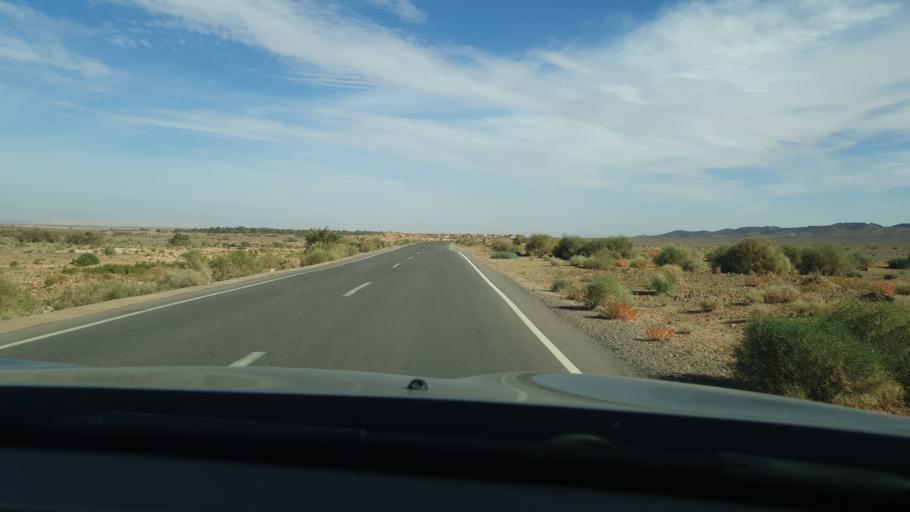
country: MA
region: Meknes-Tafilalet
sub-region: Errachidia
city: Goulmima
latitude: 31.5146
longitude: -4.9845
